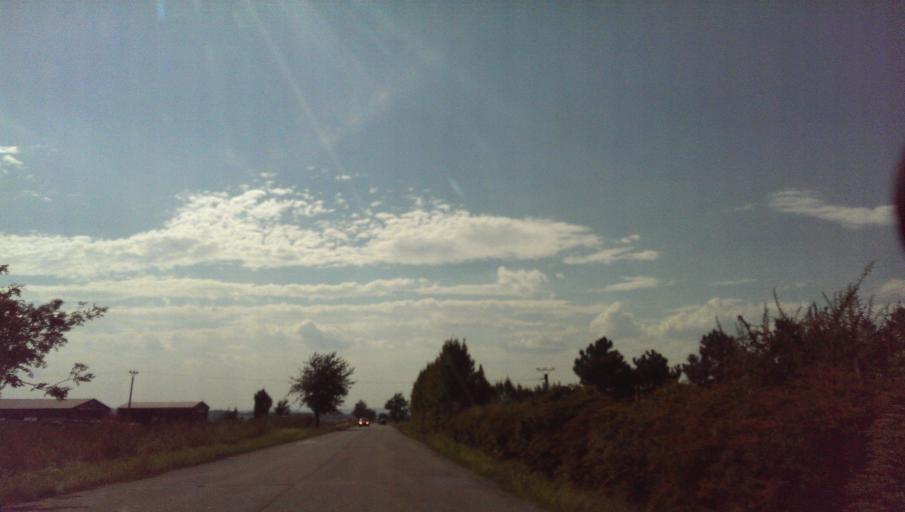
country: CZ
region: Zlin
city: Holesov
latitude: 49.3056
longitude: 17.6072
